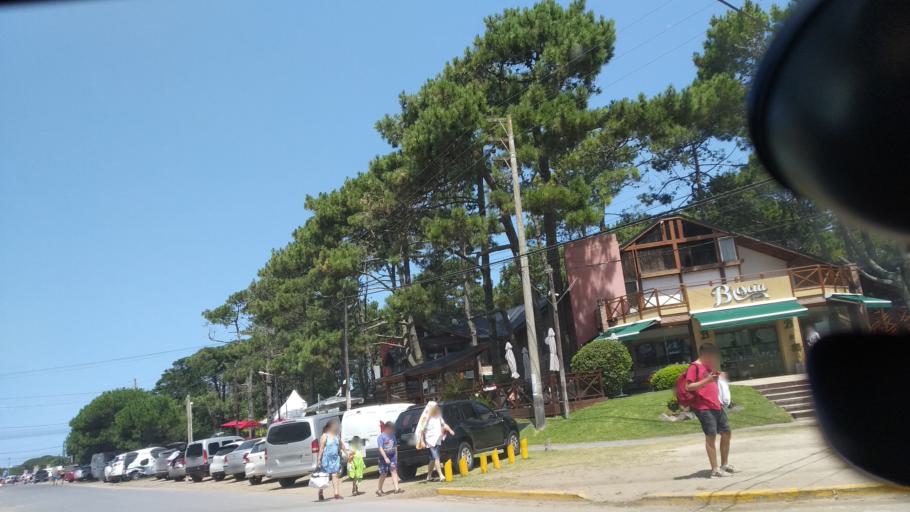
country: AR
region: Buenos Aires
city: Mar del Tuyu
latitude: -36.6064
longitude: -56.6884
